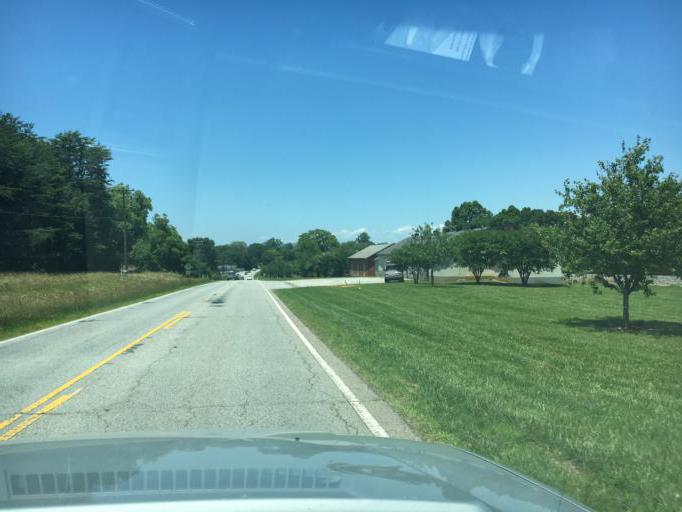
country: US
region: South Carolina
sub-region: Spartanburg County
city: Inman Mills
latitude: 35.0704
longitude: -82.1297
